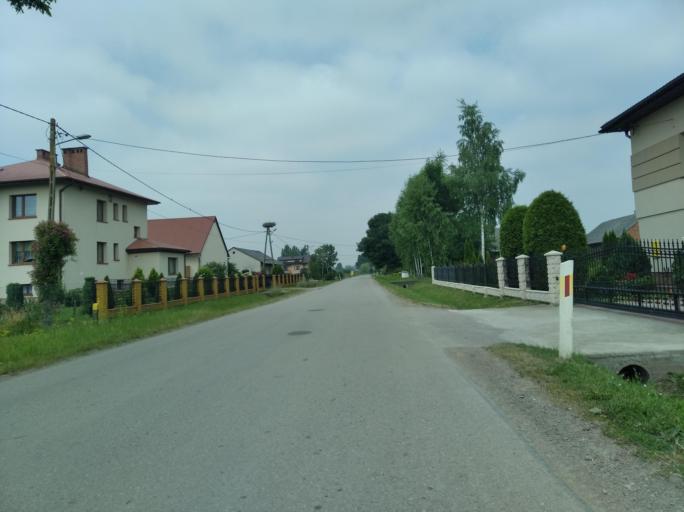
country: PL
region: Subcarpathian Voivodeship
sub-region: Powiat sanocki
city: Besko
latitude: 49.6174
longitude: 21.9443
